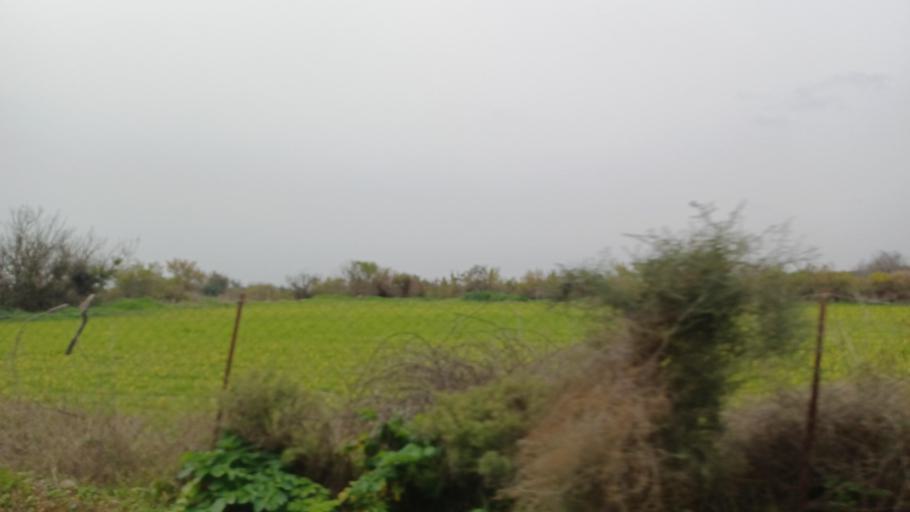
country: CY
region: Limassol
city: Pissouri
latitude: 34.7327
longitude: 32.7368
